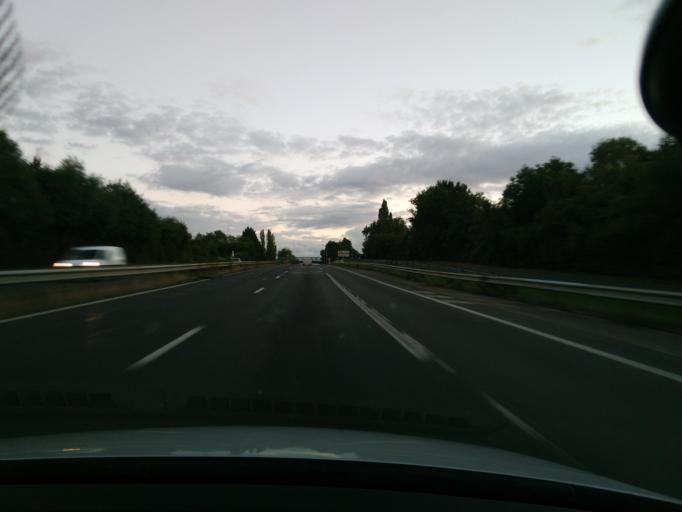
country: FR
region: Ile-de-France
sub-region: Departement de Seine-et-Marne
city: Nanteuil-les-Meaux
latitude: 48.9314
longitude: 2.8800
